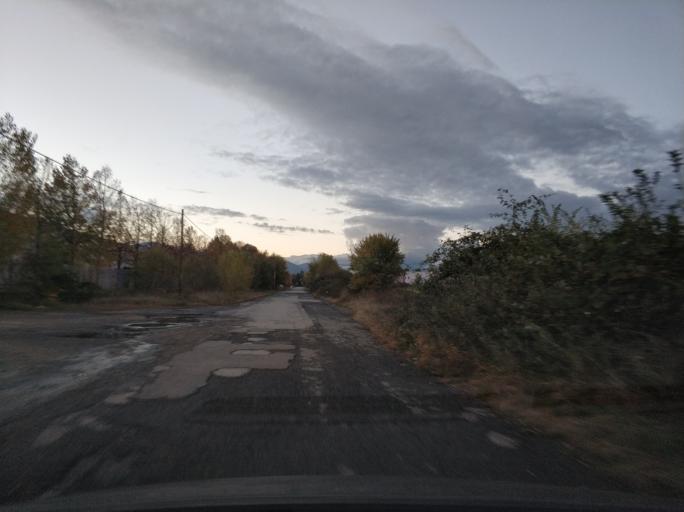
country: IT
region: Piedmont
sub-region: Provincia di Torino
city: Robassomero
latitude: 45.1754
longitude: 7.5948
